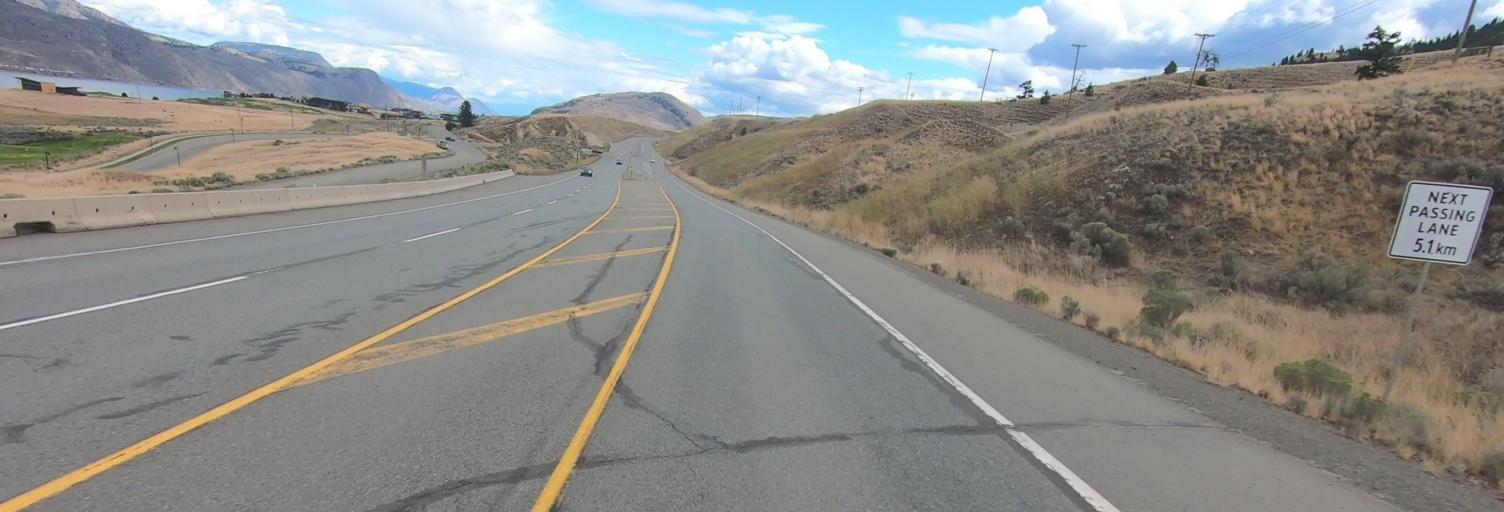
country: CA
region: British Columbia
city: Logan Lake
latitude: 50.7328
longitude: -120.6981
